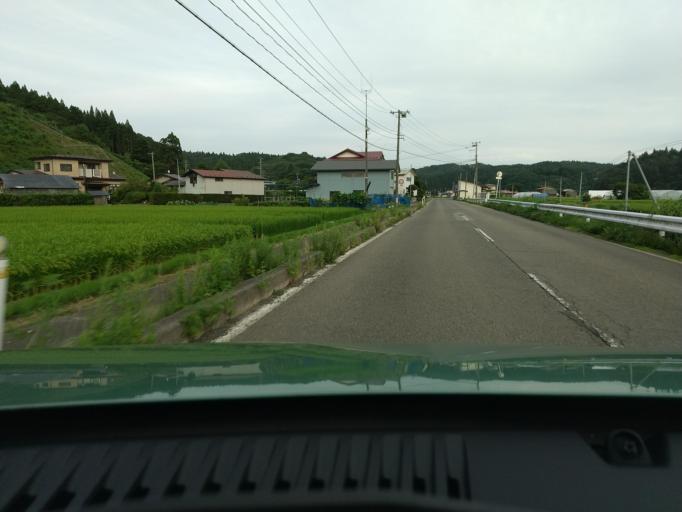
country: JP
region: Akita
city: Akita
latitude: 39.7831
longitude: 140.1273
